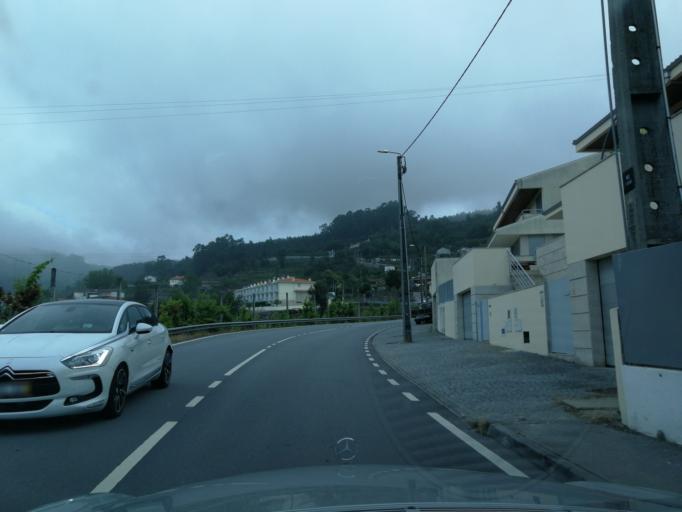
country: PT
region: Braga
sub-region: Guimaraes
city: Ponte
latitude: 41.5165
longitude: -8.3572
